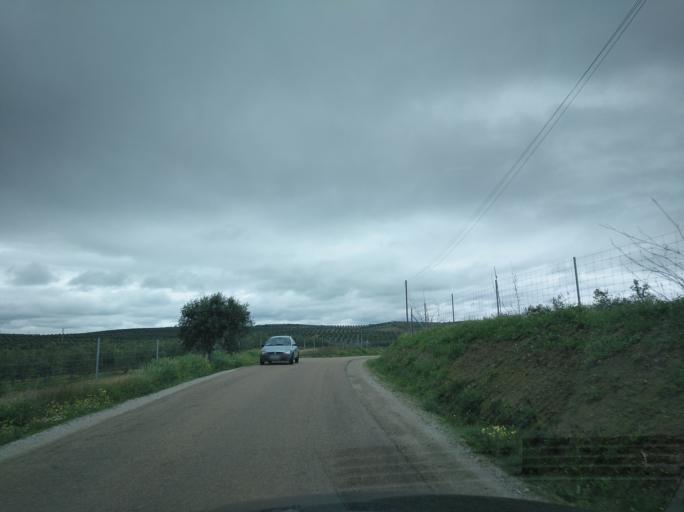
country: PT
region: Portalegre
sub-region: Campo Maior
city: Campo Maior
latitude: 39.0037
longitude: -7.0579
